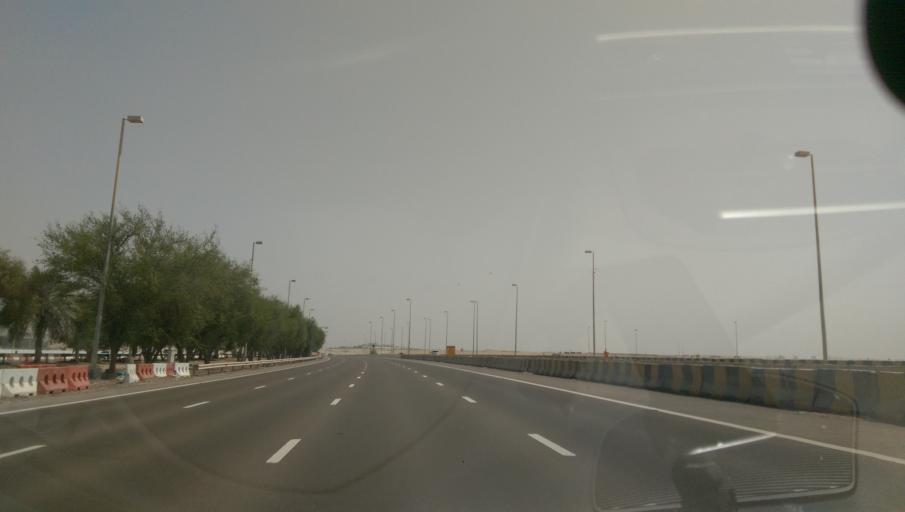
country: AE
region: Abu Dhabi
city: Abu Dhabi
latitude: 24.4190
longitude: 54.6772
